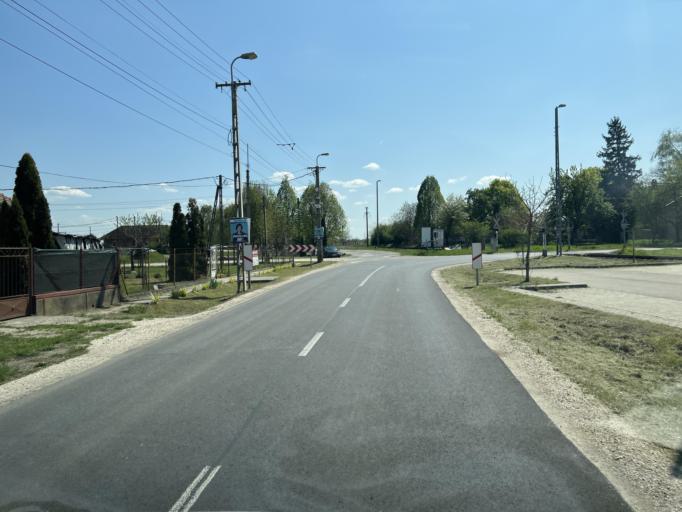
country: HU
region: Pest
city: Inarcs
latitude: 47.2458
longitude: 19.3198
